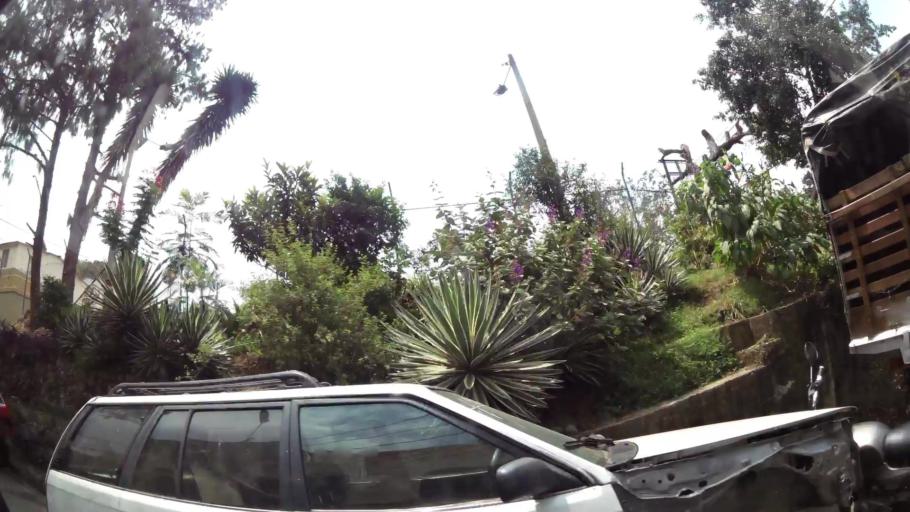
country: CO
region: Antioquia
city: Medellin
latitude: 6.2612
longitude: -75.5481
